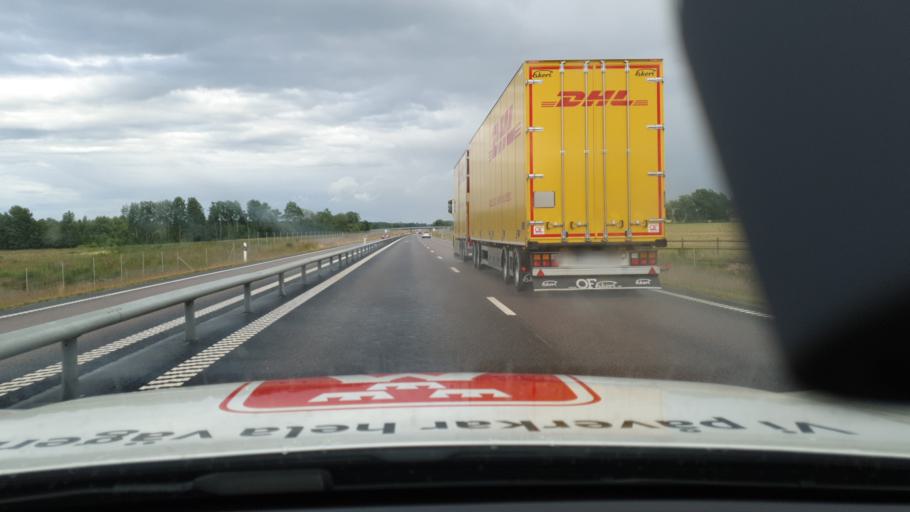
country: SE
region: Vaestra Goetaland
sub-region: Lidkopings Kommun
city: Vinninga
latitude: 58.4790
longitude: 13.2213
